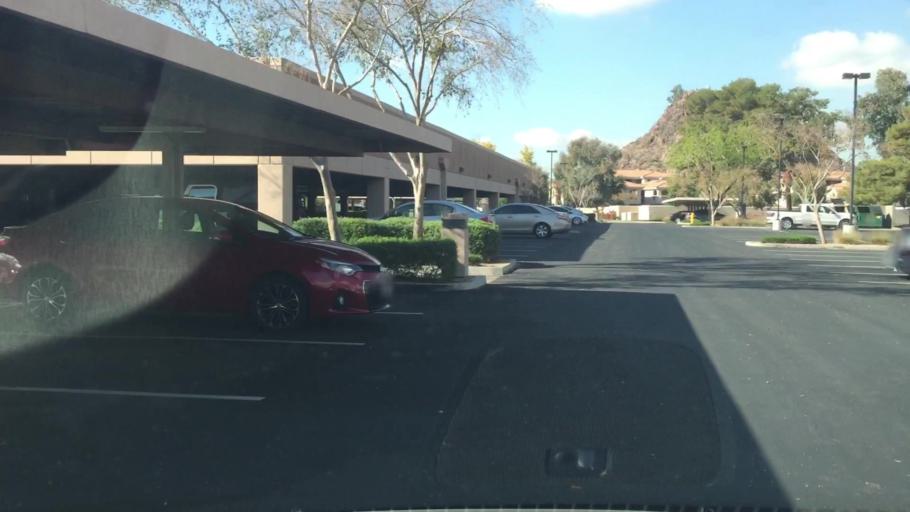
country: US
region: Arizona
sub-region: Maricopa County
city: Tempe Junction
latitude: 33.4052
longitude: -111.9622
